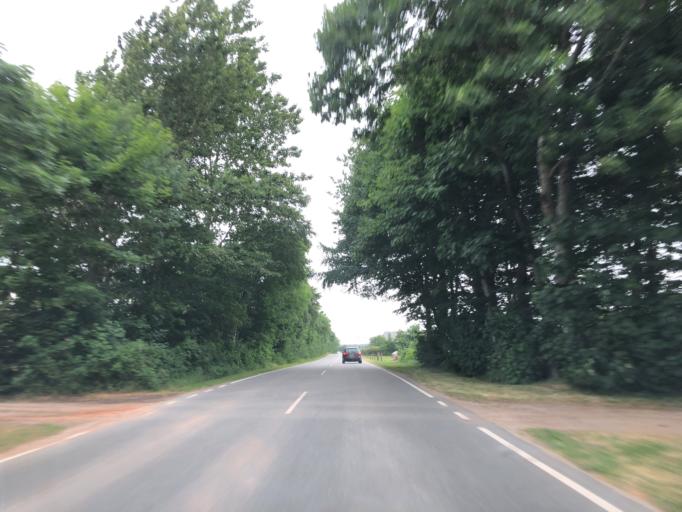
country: DK
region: Central Jutland
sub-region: Holstebro Kommune
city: Holstebro
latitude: 56.2666
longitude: 8.6451
